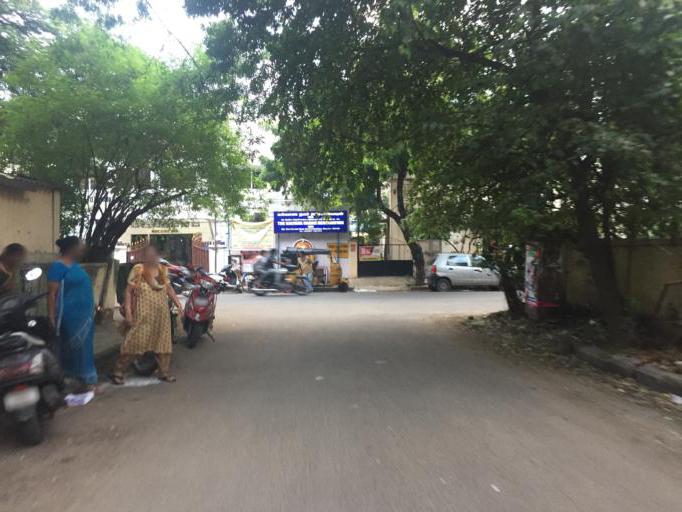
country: IN
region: Tamil Nadu
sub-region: Chennai
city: Gandhi Nagar
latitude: 13.0289
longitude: 80.2700
